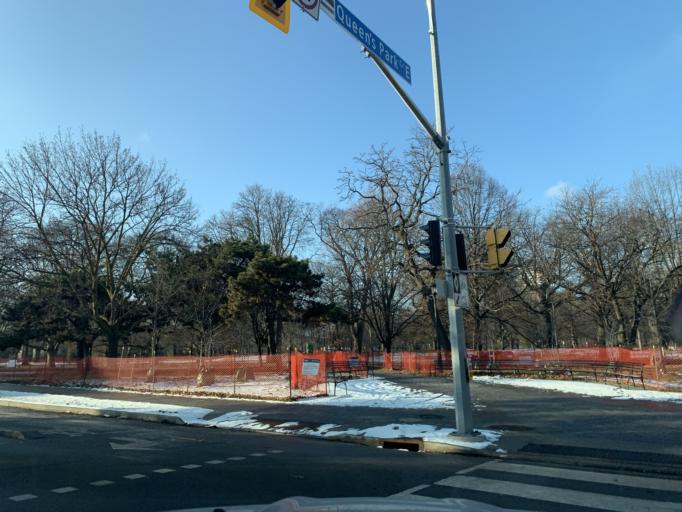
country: CA
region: Ontario
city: Toronto
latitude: 43.6636
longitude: -79.3907
